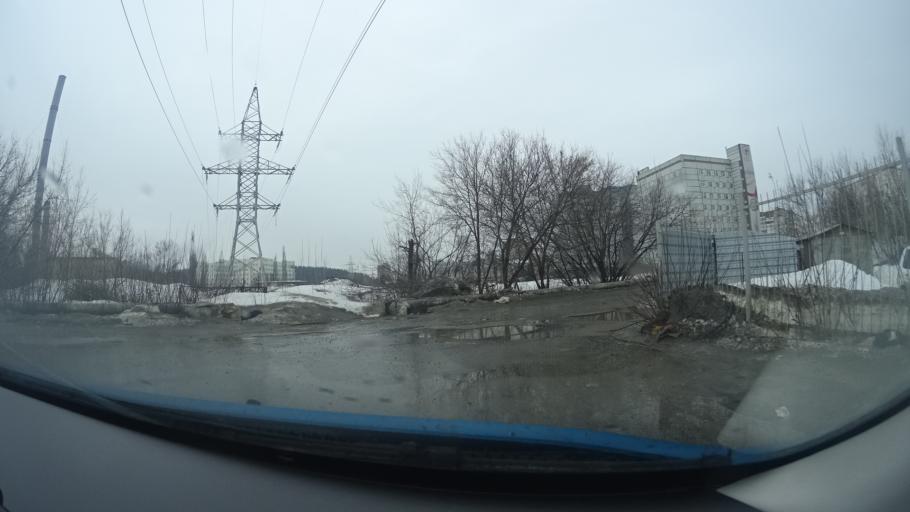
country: RU
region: Bashkortostan
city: Ufa
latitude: 54.7117
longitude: 56.0098
